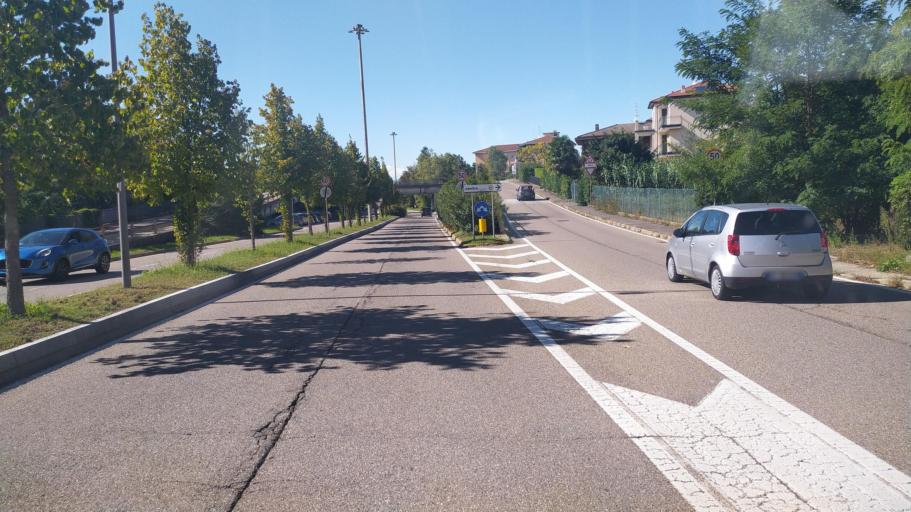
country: IT
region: Lombardy
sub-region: Provincia di Varese
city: Varese
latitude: 45.8115
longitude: 8.8248
